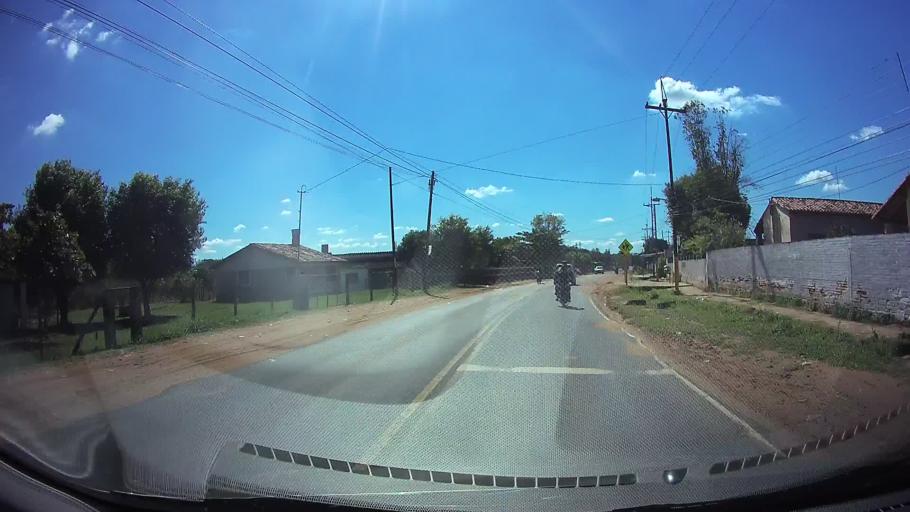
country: PY
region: Central
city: Limpio
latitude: -25.2000
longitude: -57.4648
